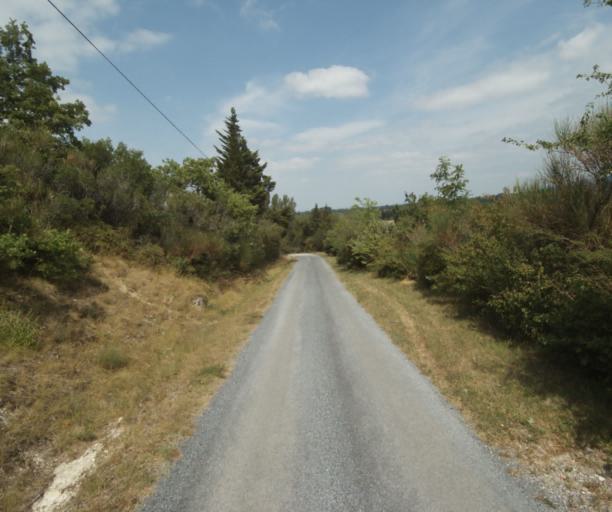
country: FR
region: Midi-Pyrenees
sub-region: Departement du Tarn
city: Soreze
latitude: 43.4464
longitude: 2.0462
